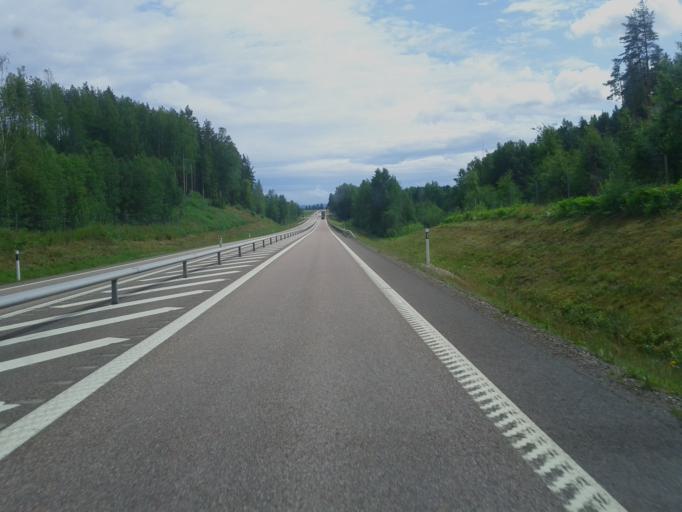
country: SE
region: Dalarna
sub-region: Hedemora Kommun
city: Hedemora
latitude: 60.3190
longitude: 15.9117
